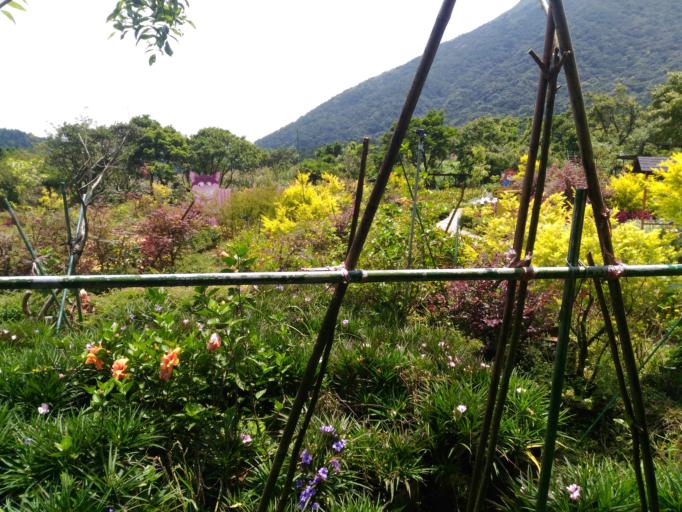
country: TW
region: Taipei
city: Taipei
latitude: 25.1755
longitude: 121.5337
